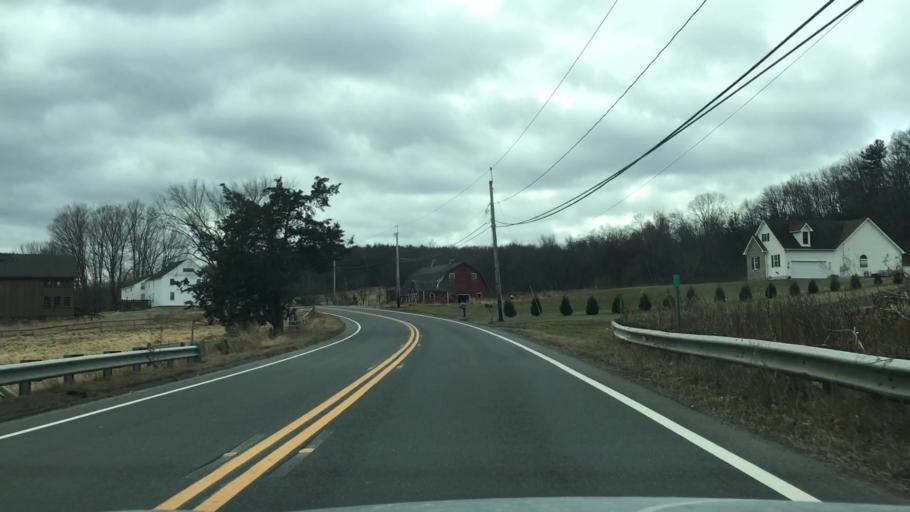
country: US
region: Connecticut
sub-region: Hartford County
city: North Granby
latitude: 42.0138
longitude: -72.7946
